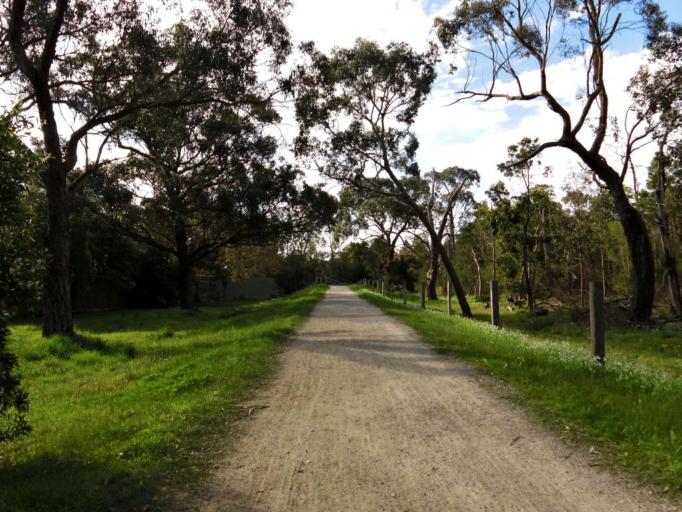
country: AU
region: Victoria
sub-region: Whitehorse
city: Vermont South
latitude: -37.8819
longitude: 145.1901
